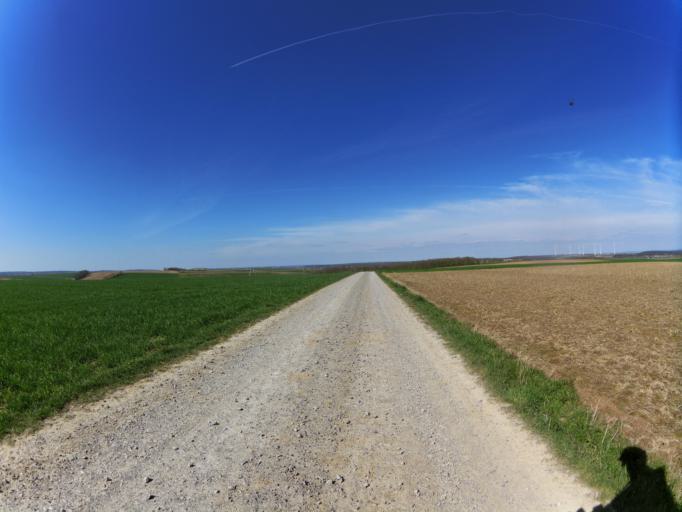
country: DE
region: Bavaria
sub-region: Regierungsbezirk Unterfranken
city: Winterhausen
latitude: 49.6857
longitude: 9.9991
